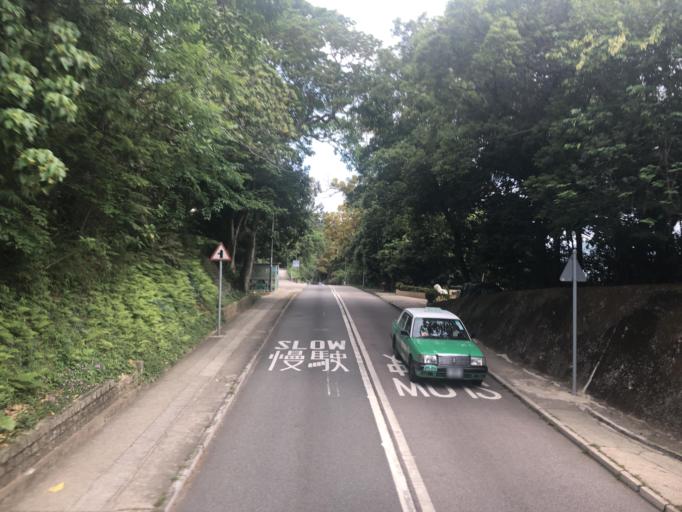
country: HK
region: Sai Kung
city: Sai Kung
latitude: 22.3959
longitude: 114.2869
